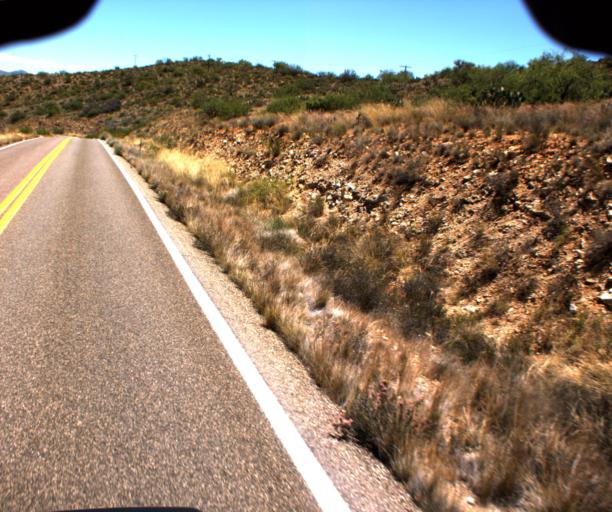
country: US
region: Arizona
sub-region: Yavapai County
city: Bagdad
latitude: 34.5211
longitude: -113.1032
